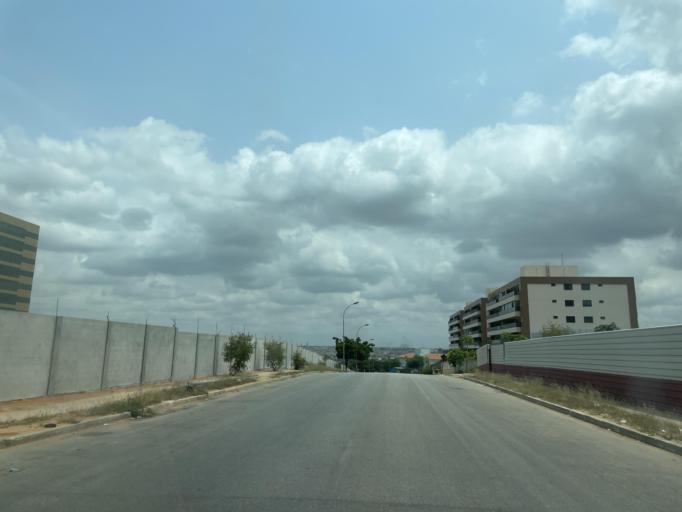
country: AO
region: Luanda
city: Luanda
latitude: -8.9242
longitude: 13.1880
